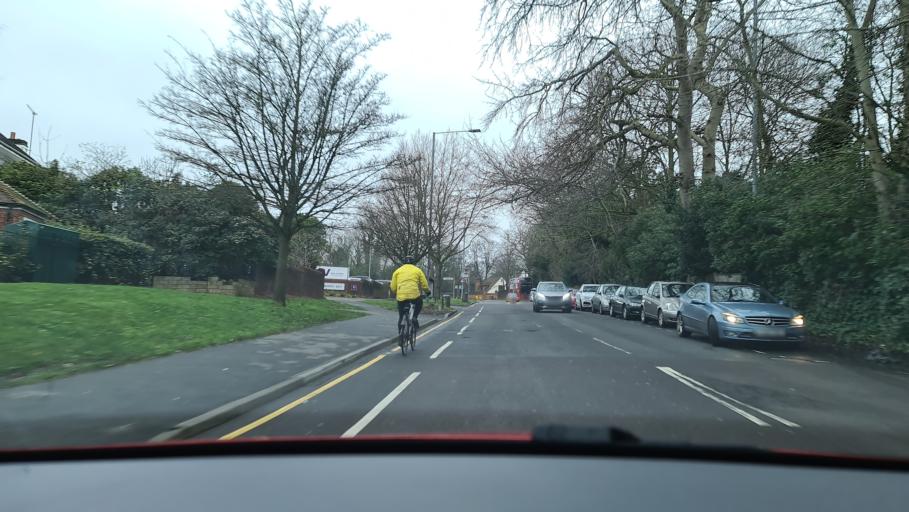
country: GB
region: England
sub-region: Greater London
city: New Malden
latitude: 51.4160
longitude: -0.2529
